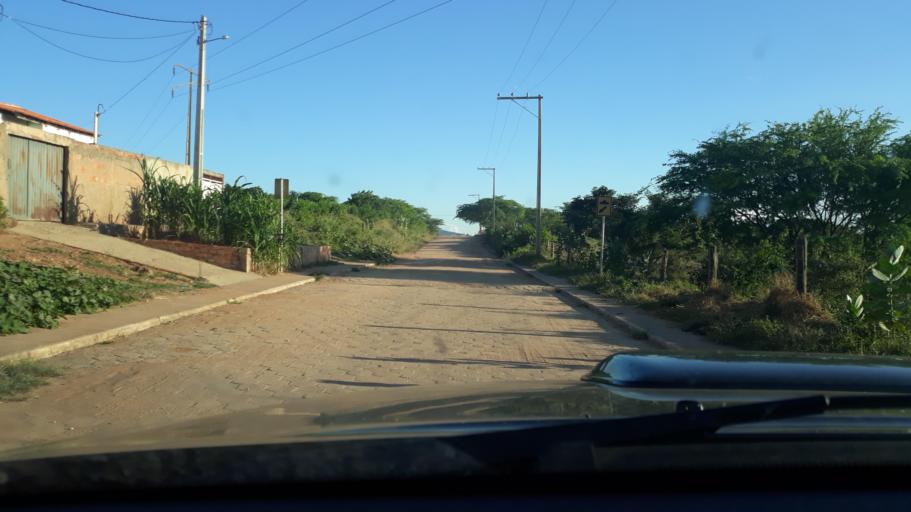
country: BR
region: Bahia
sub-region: Riacho De Santana
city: Riacho de Santana
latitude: -13.7846
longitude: -42.7136
